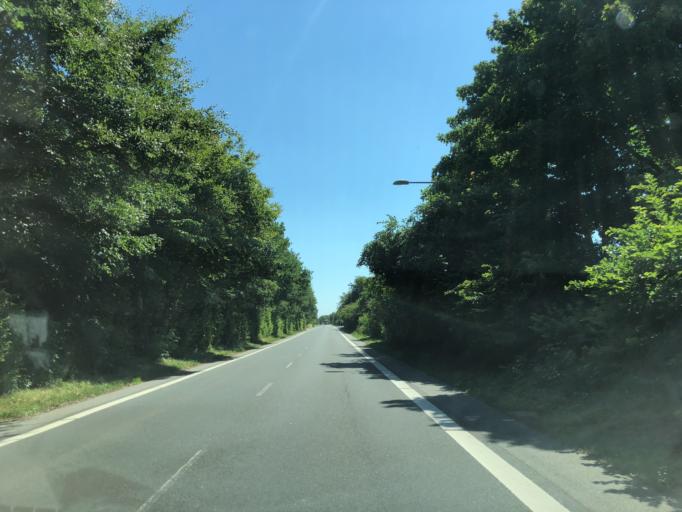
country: DK
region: Central Jutland
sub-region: Holstebro Kommune
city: Holstebro
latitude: 56.3461
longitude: 8.6558
